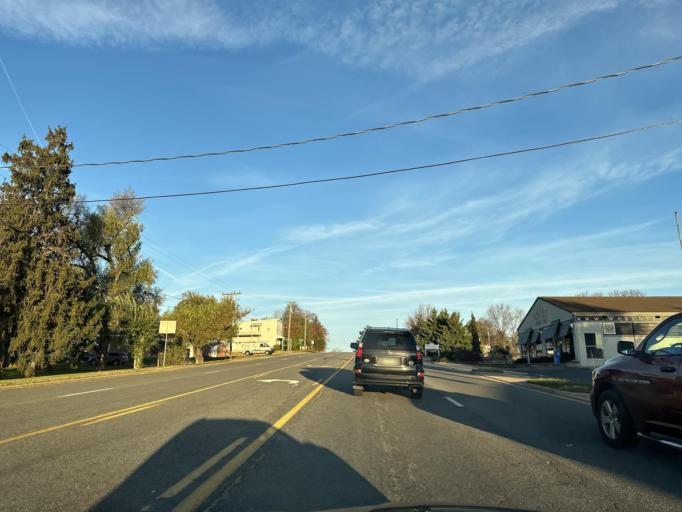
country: US
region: Virginia
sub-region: Augusta County
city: Fishersville
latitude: 38.0994
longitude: -78.9699
